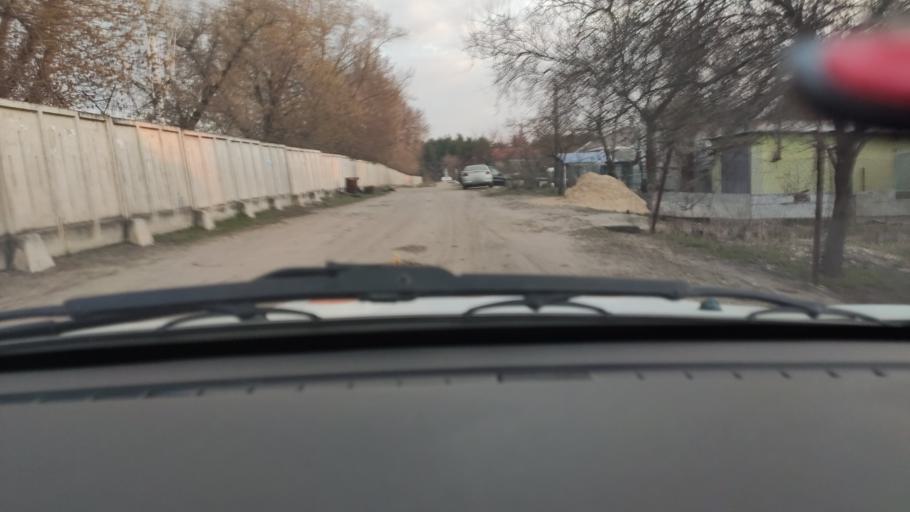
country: RU
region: Voronezj
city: Maslovka
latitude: 51.6074
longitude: 39.2246
